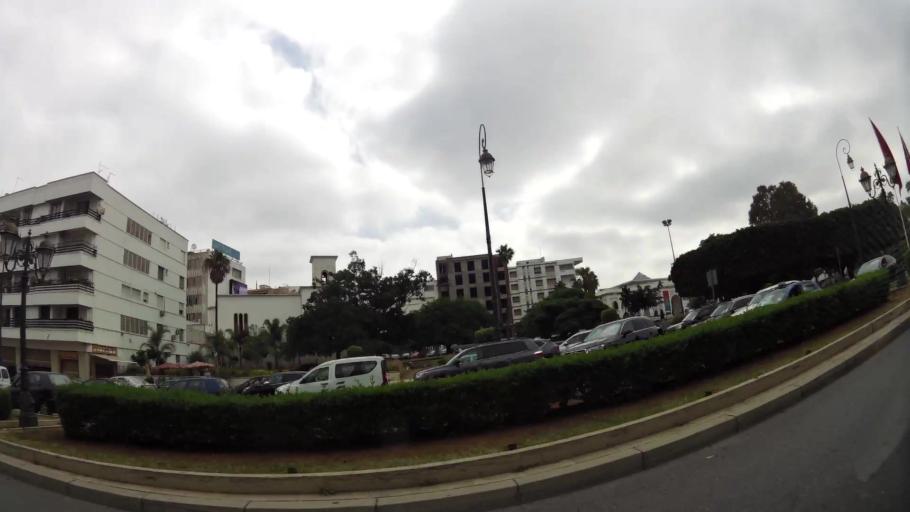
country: MA
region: Rabat-Sale-Zemmour-Zaer
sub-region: Rabat
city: Rabat
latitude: 34.0153
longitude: -6.8347
